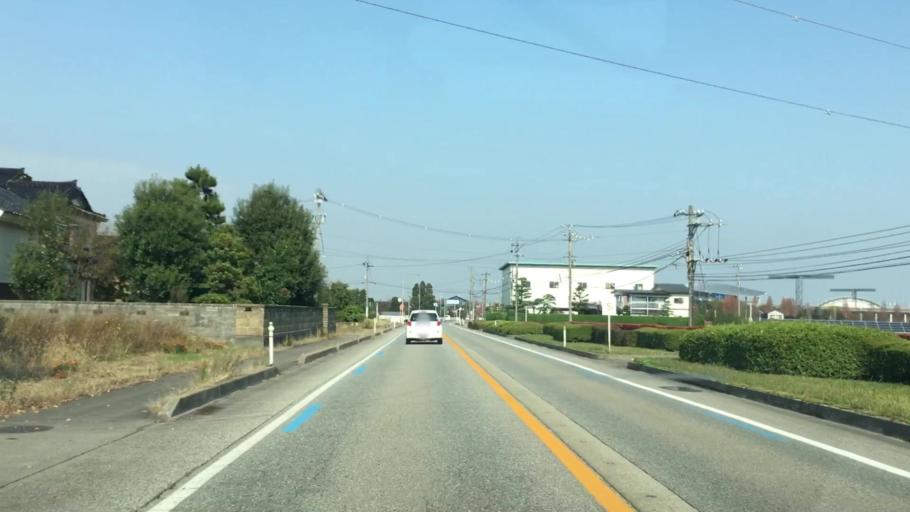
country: JP
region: Toyama
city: Toyama-shi
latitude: 36.6196
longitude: 137.1930
